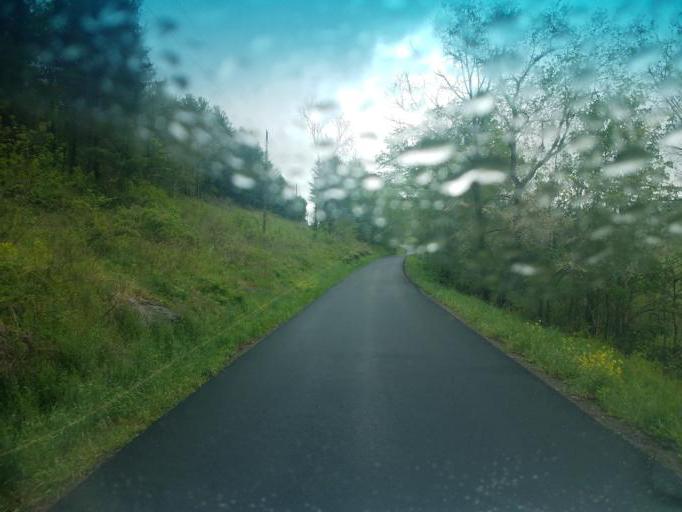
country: US
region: Virginia
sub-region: Smyth County
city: Marion
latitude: 36.9281
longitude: -81.5427
